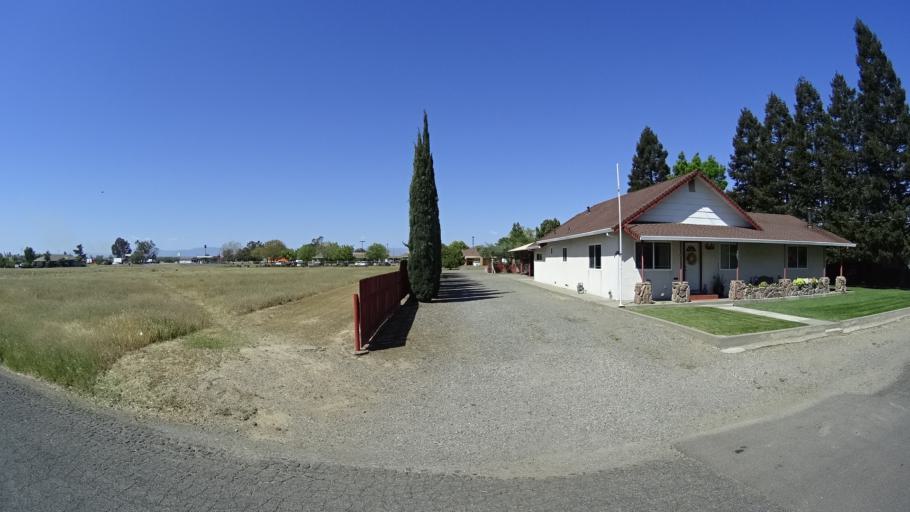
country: US
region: California
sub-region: Glenn County
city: Orland
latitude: 39.7418
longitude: -122.1995
